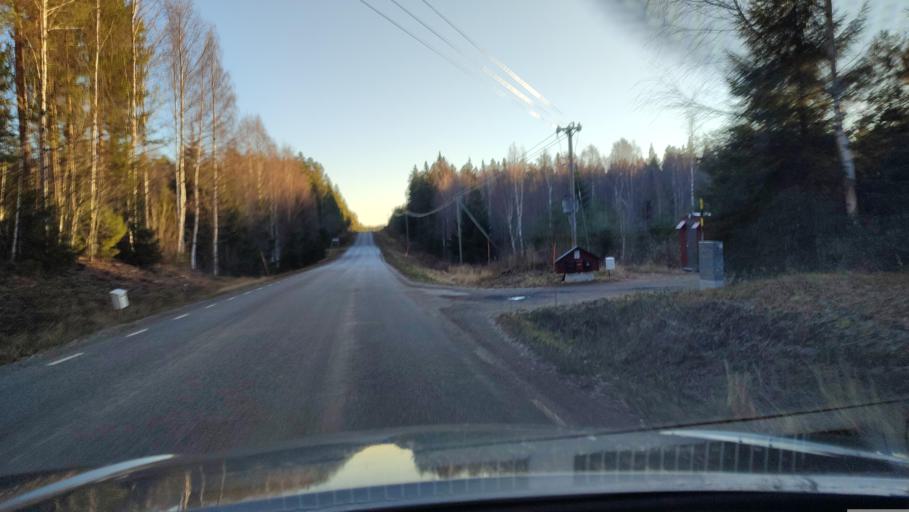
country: SE
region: Vaesterbotten
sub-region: Skelleftea Kommun
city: Viken
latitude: 64.6960
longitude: 20.9242
